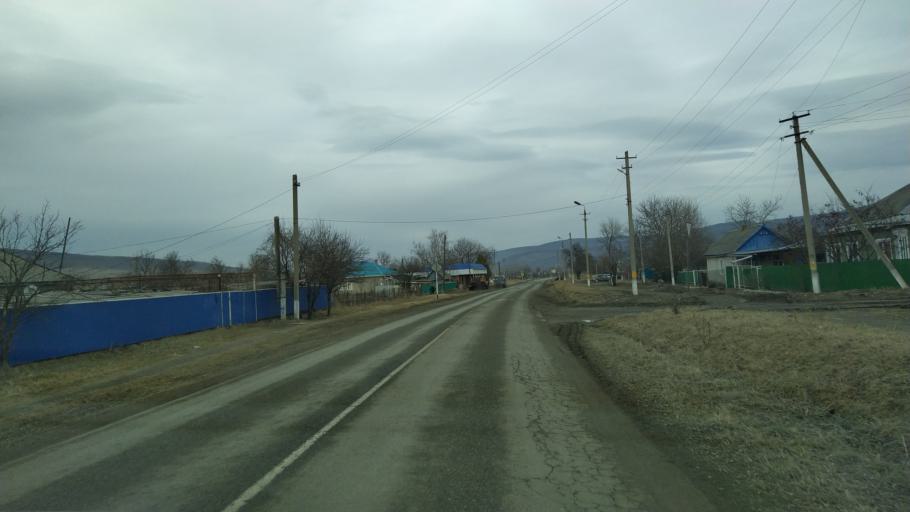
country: RU
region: Krasnodarskiy
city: Peredovaya
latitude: 44.1274
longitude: 41.4813
